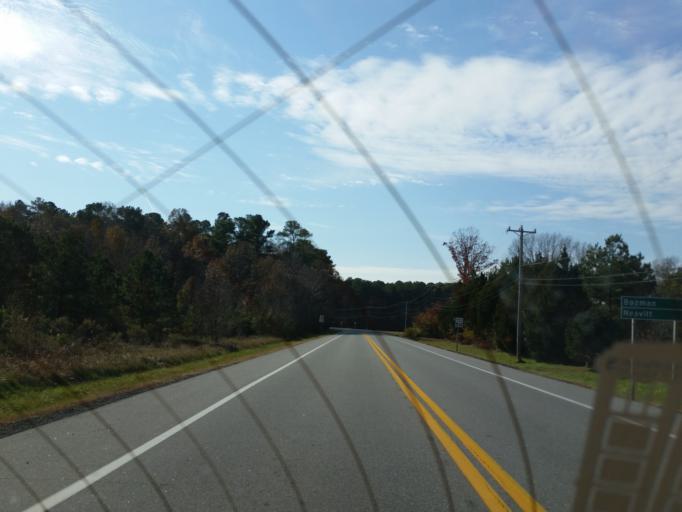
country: US
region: Maryland
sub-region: Talbot County
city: Saint Michaels
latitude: 38.8121
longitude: -76.2501
